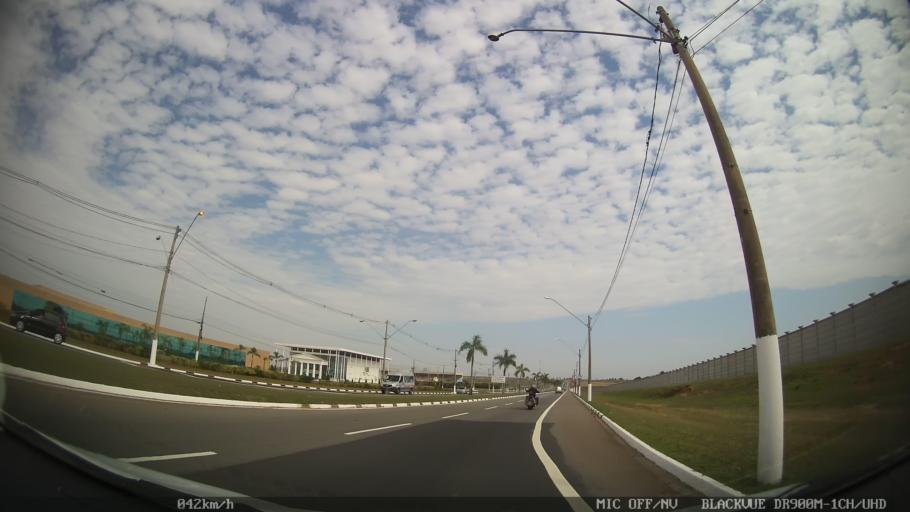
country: BR
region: Sao Paulo
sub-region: Paulinia
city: Paulinia
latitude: -22.7834
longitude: -47.1596
